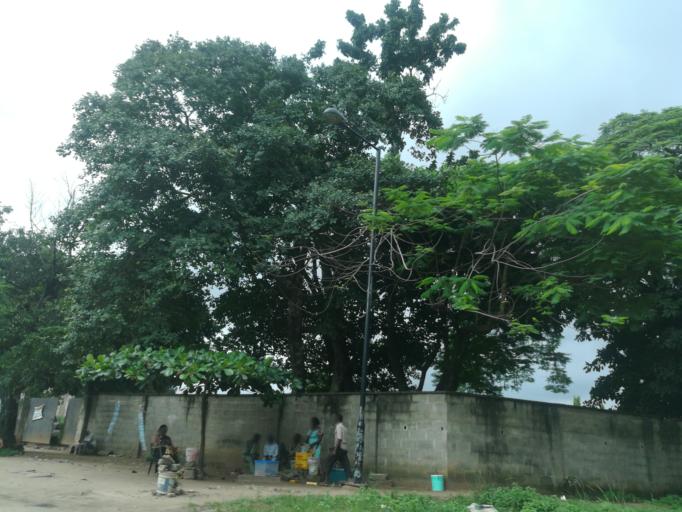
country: NG
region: Lagos
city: Oshodi
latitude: 6.5774
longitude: 3.3554
